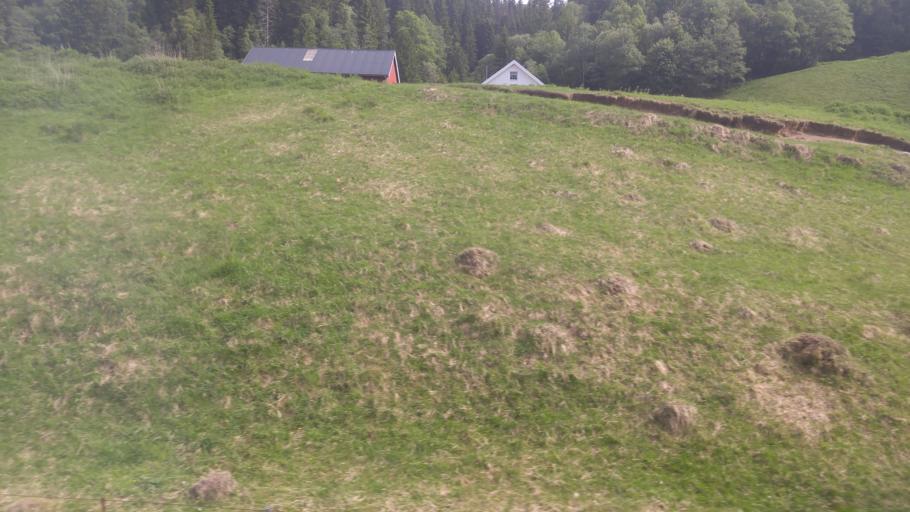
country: NO
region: Sor-Trondelag
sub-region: Midtre Gauldal
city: Storen
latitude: 63.0018
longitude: 10.4626
